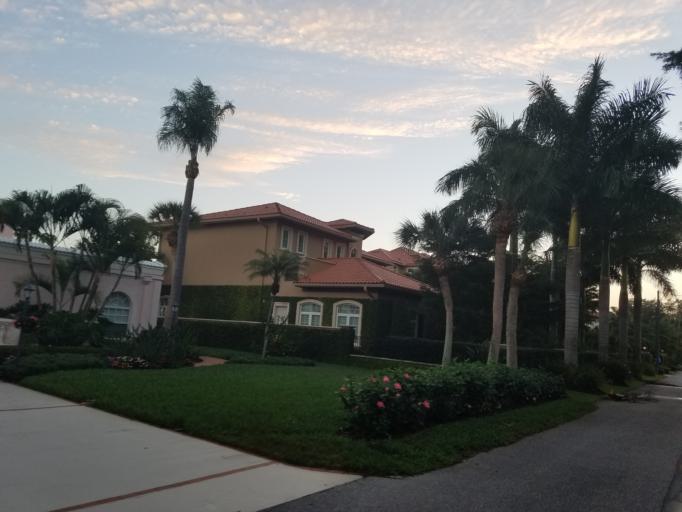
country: US
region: Florida
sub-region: Sarasota County
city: Siesta Key
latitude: 27.3041
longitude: -82.5502
